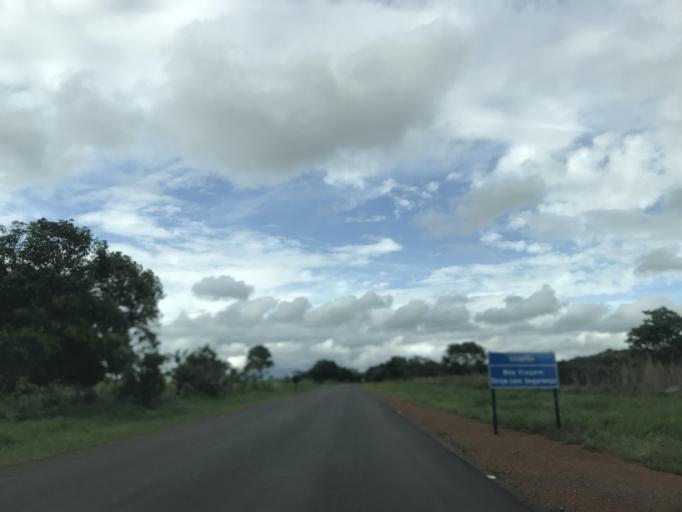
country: BR
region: Goias
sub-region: Bela Vista De Goias
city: Bela Vista de Goias
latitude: -17.0436
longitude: -48.6636
